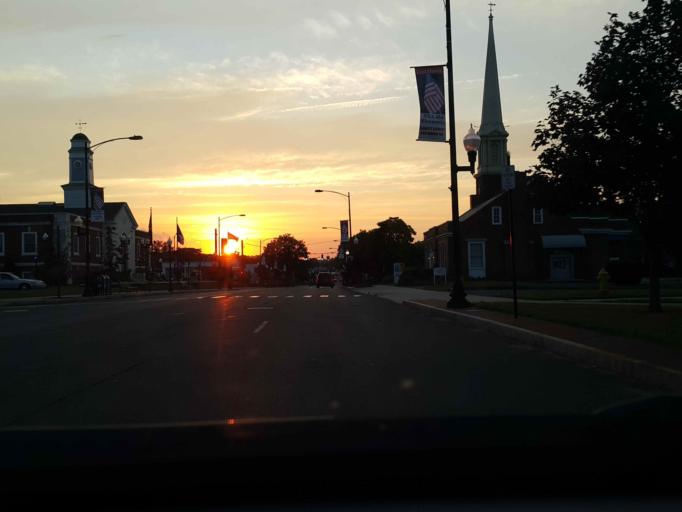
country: US
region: Connecticut
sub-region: New Haven County
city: East Haven
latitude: 41.2775
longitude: -72.8706
